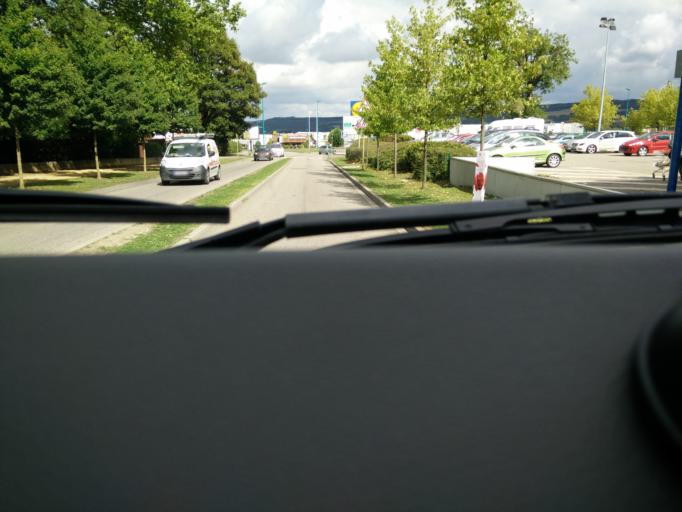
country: FR
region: Lorraine
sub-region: Departement de la Meuse
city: Verdun
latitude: 49.1442
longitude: 5.4086
